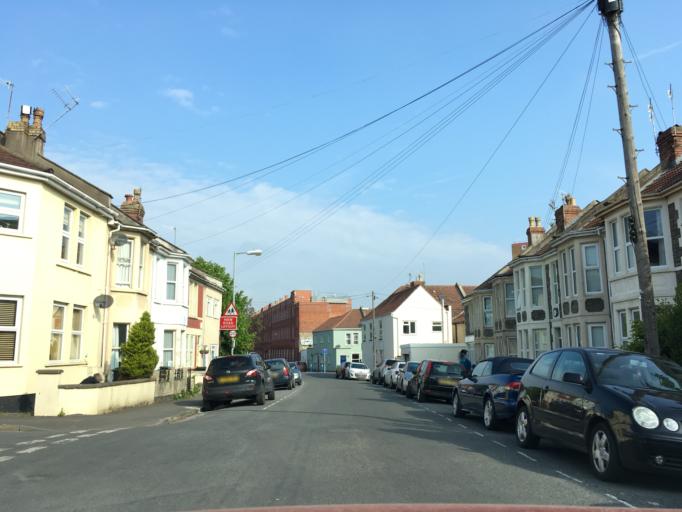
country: GB
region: England
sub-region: Bristol
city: Bristol
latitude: 51.4433
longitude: -2.6101
